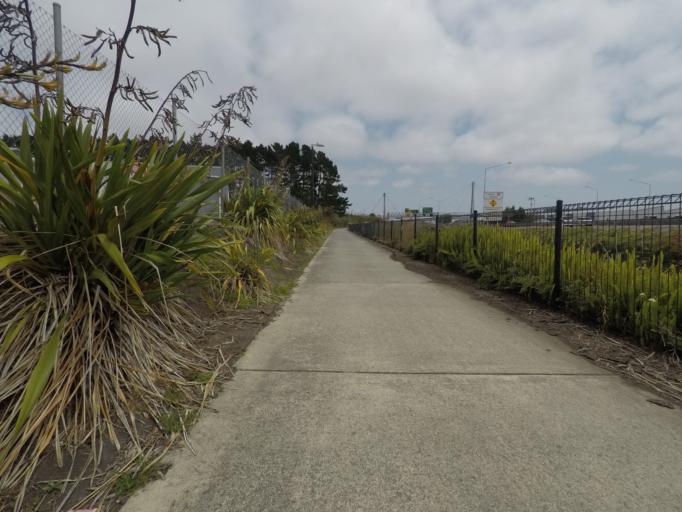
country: NZ
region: Auckland
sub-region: Auckland
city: Auckland
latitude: -36.9072
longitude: 174.7290
